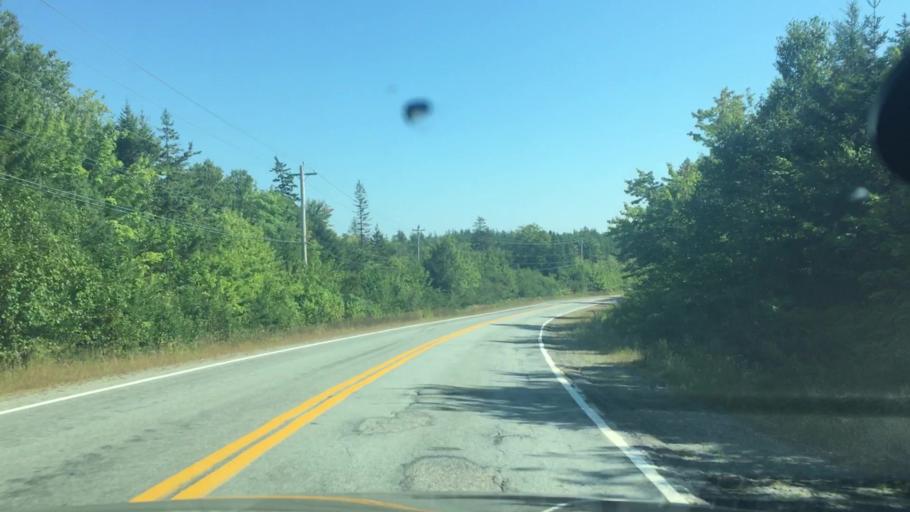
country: CA
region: Nova Scotia
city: New Glasgow
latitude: 44.9099
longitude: -62.5527
